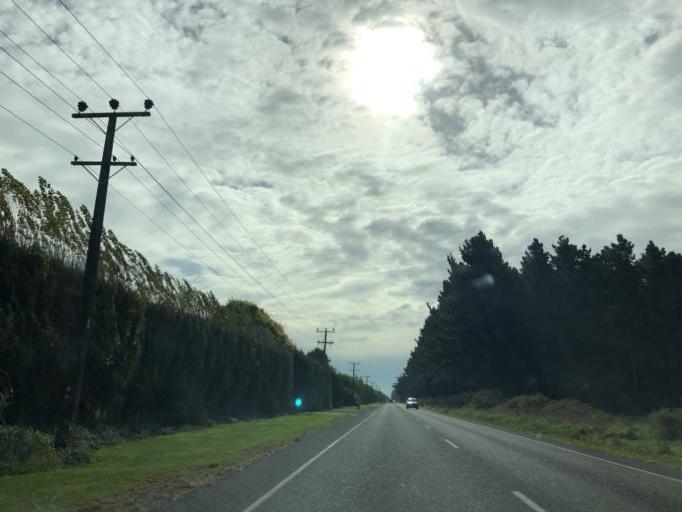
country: NZ
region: Canterbury
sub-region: Selwyn District
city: Lincoln
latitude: -43.6343
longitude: 172.4435
